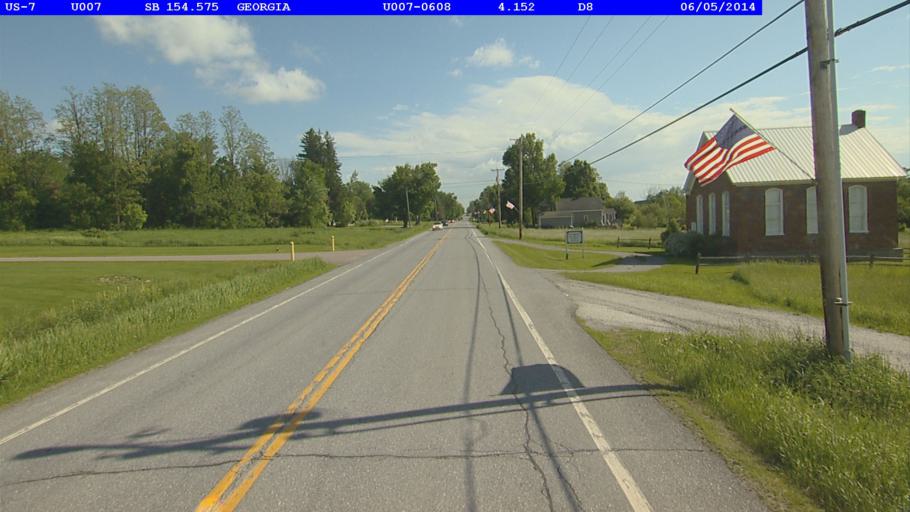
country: US
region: Vermont
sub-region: Franklin County
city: Saint Albans
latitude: 44.7312
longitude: -73.1170
